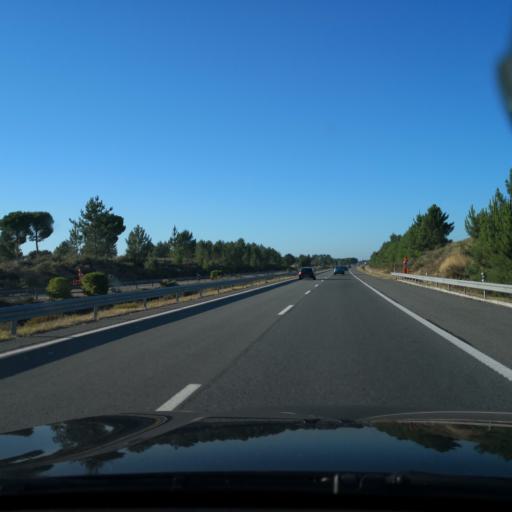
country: PT
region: Setubal
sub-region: Grandola
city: Grandola
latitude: 38.2149
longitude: -8.5161
